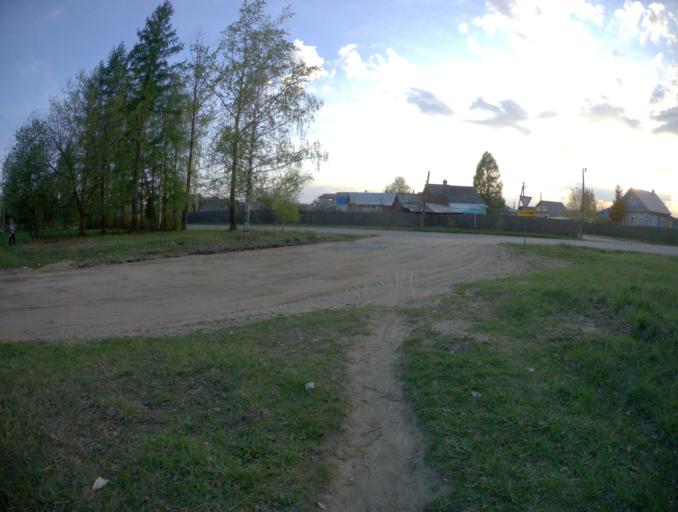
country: RU
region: Ivanovo
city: Yuzha
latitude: 56.5750
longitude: 42.0166
